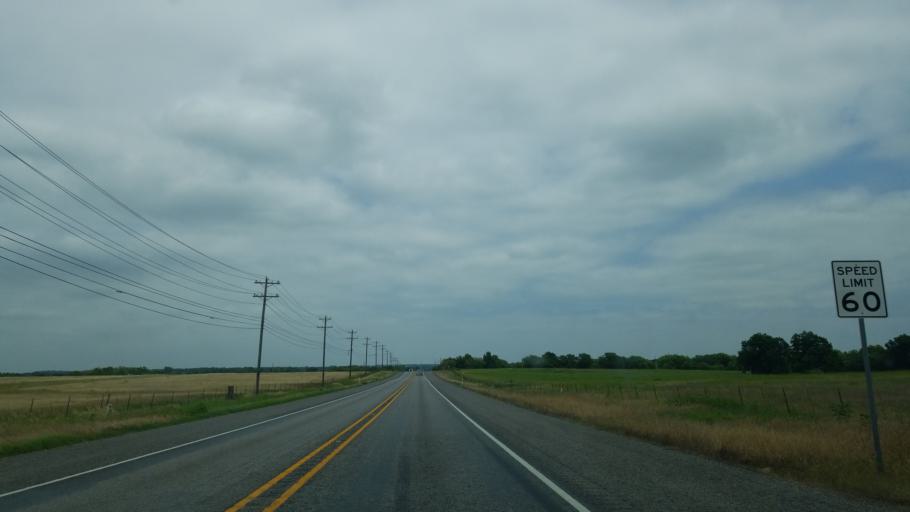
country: US
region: Texas
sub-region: Denton County
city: Aubrey
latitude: 33.3073
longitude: -97.0563
